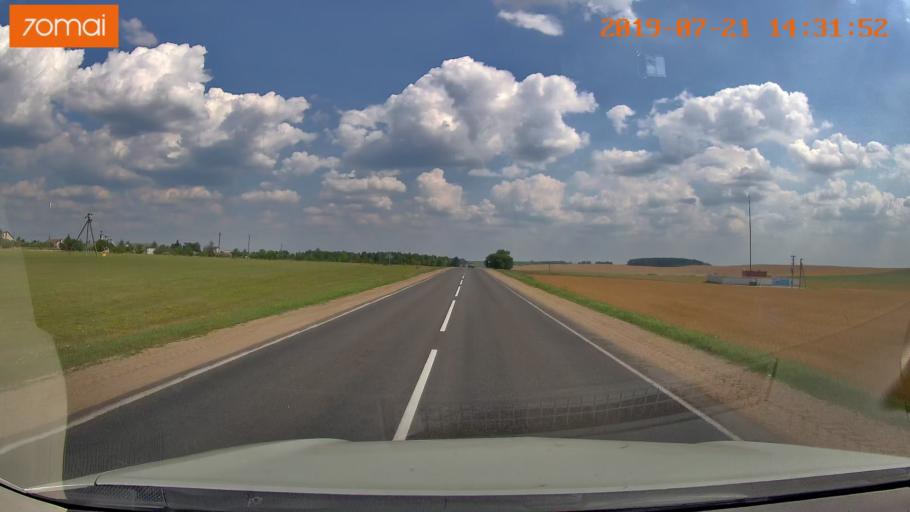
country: BY
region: Grodnenskaya
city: Karelichy
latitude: 53.5229
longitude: 26.3019
